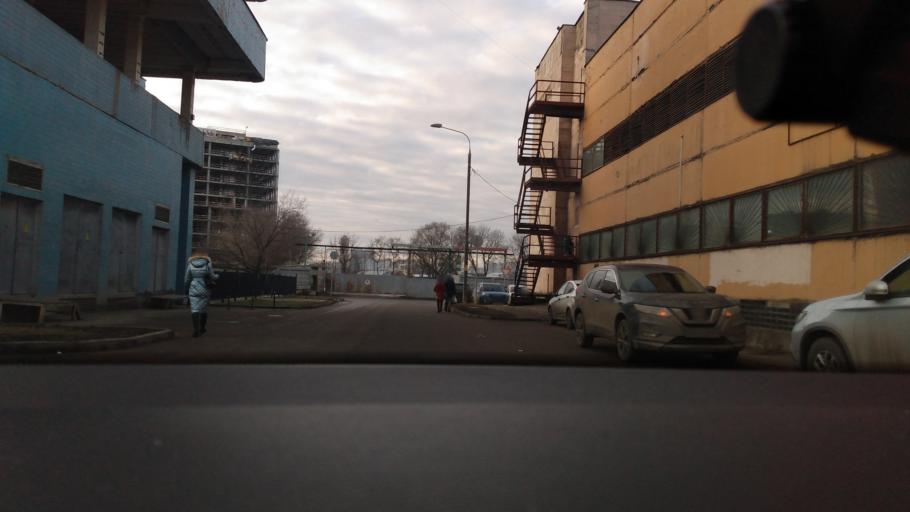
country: RU
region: Moscow
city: Strogino
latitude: 55.8251
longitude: 37.4251
